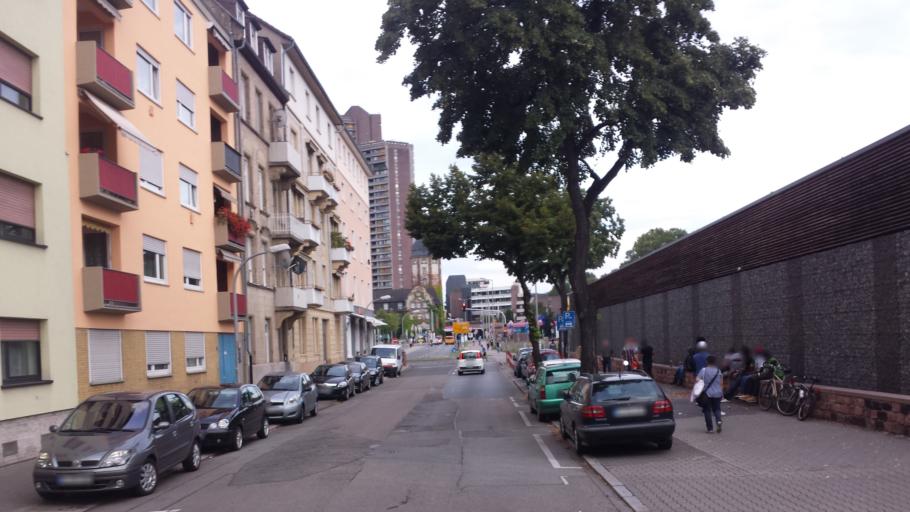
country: DE
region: Baden-Wuerttemberg
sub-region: Karlsruhe Region
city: Mannheim
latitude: 49.4963
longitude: 8.4704
